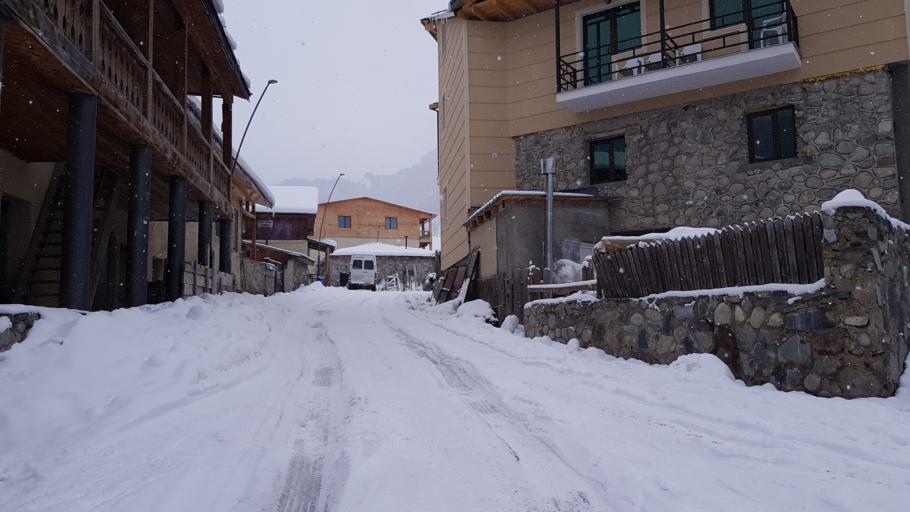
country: GE
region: Samegrelo and Zemo Svaneti
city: Mest'ia
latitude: 43.0429
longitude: 42.7273
